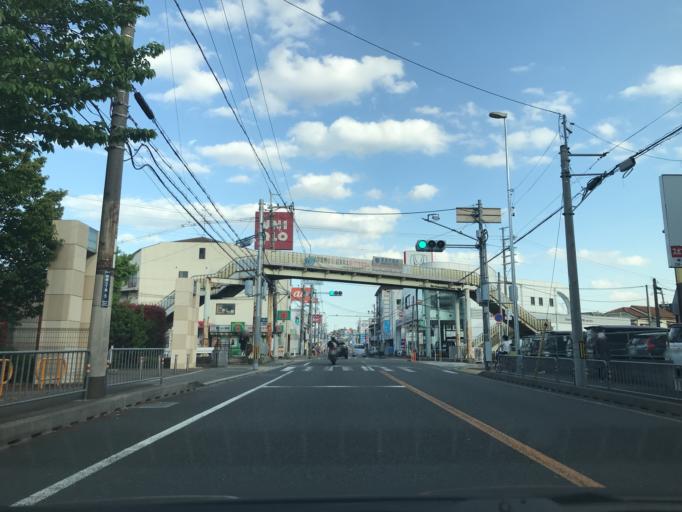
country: JP
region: Osaka
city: Ikeda
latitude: 34.8179
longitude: 135.4335
